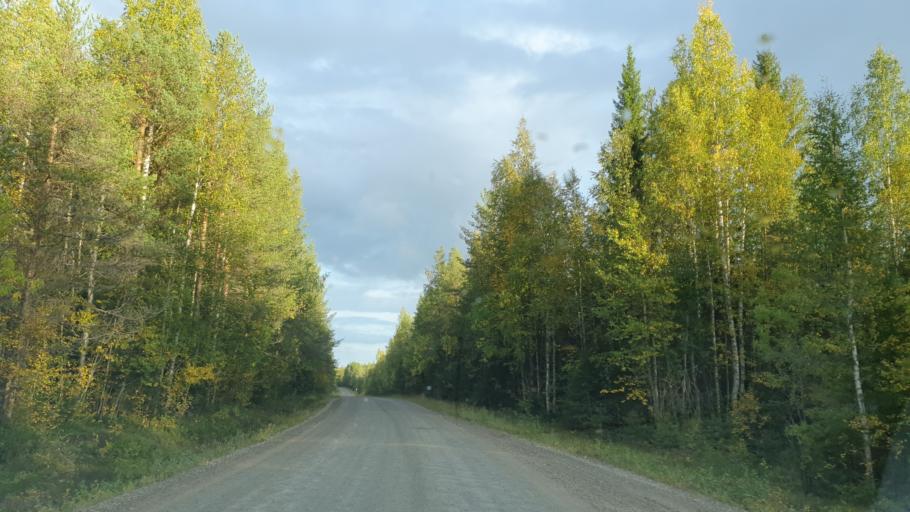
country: FI
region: Kainuu
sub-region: Kehys-Kainuu
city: Kuhmo
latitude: 64.4284
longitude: 29.3265
